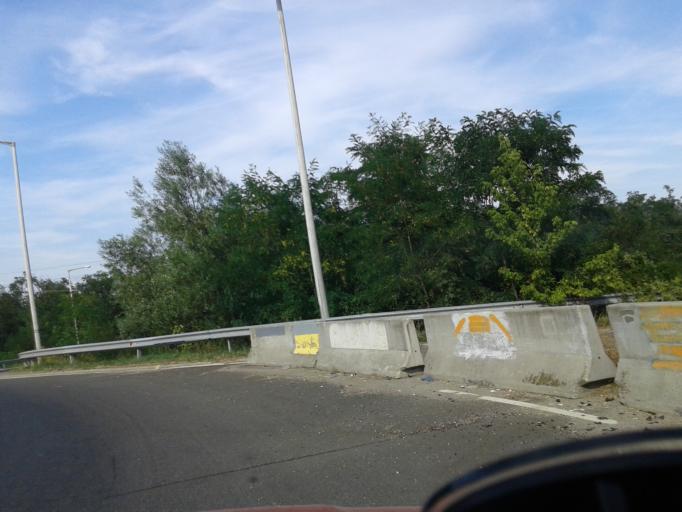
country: HU
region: Pest
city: Godollo
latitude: 47.5919
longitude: 19.3293
